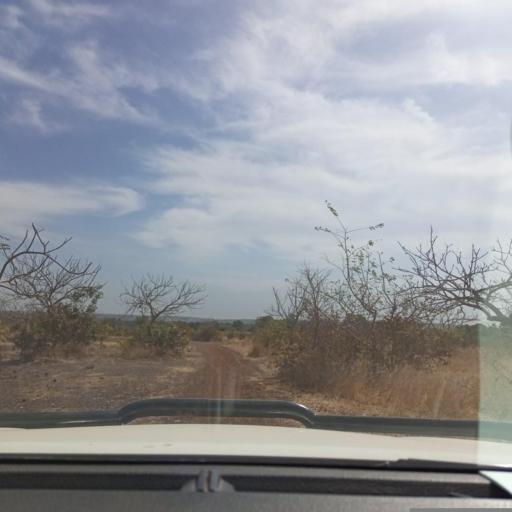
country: ML
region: Koulikoro
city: Kati
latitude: 12.7339
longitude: -8.2541
